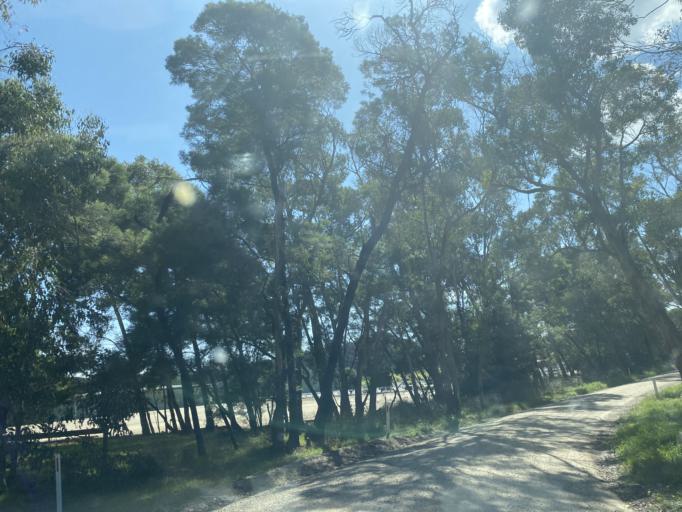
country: AU
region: Victoria
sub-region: Cardinia
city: Bunyip
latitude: -38.0481
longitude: 145.7189
